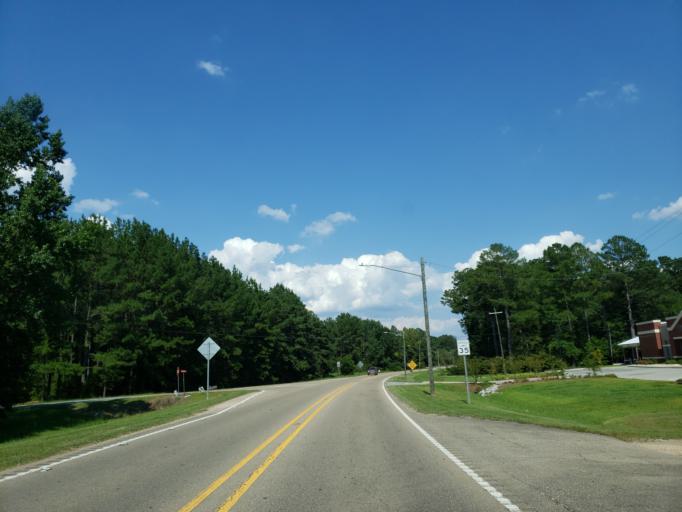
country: US
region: Mississippi
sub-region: Covington County
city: Collins
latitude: 31.5630
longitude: -89.5089
